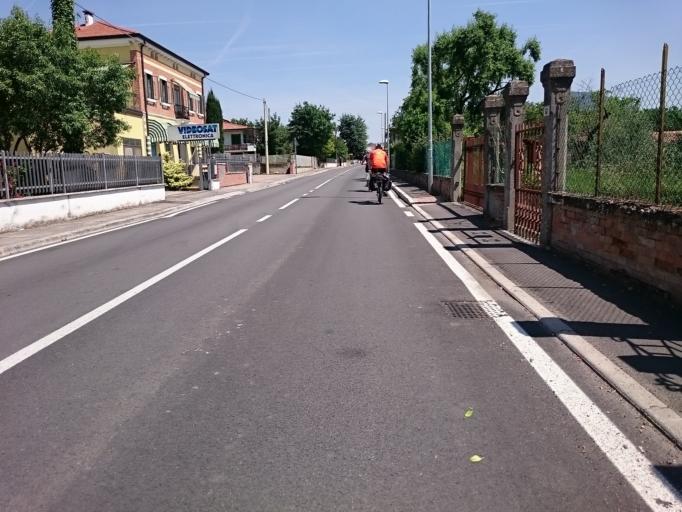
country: IT
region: Veneto
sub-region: Provincia di Padova
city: Lozzo Atestino
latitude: 45.2884
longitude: 11.6274
